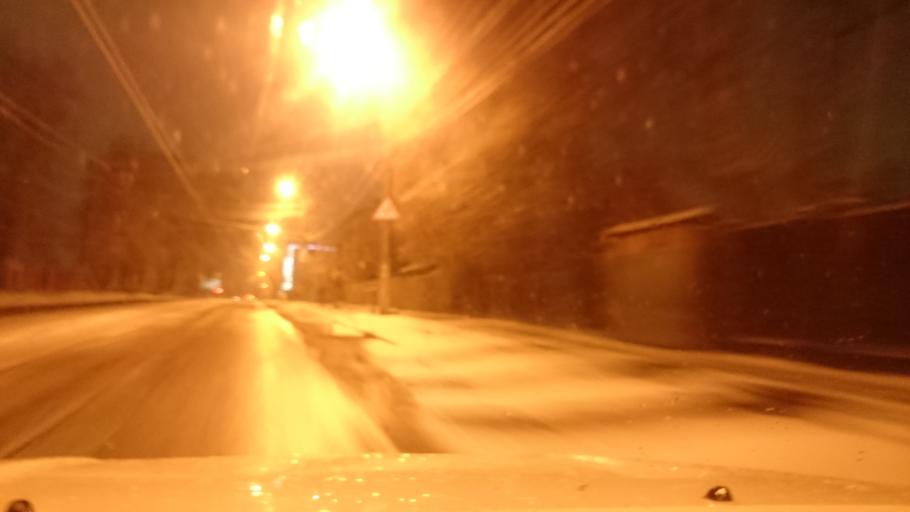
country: RU
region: Tula
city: Mendeleyevskiy
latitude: 54.1709
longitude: 37.5847
